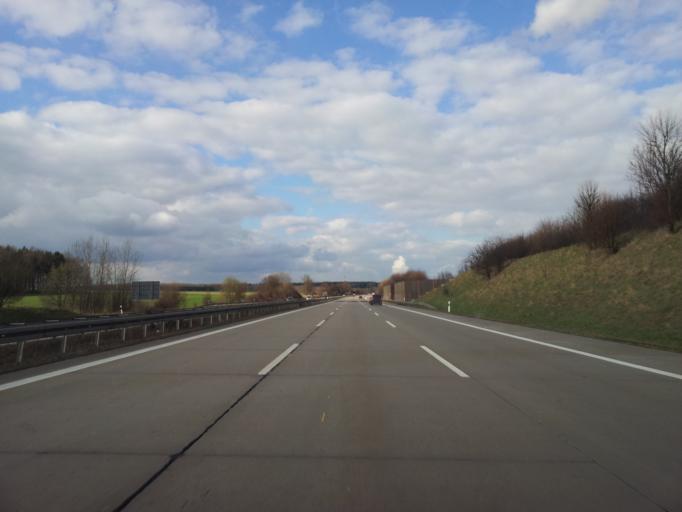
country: DE
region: Saxony
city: Frankenberg
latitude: 50.9415
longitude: 13.0629
